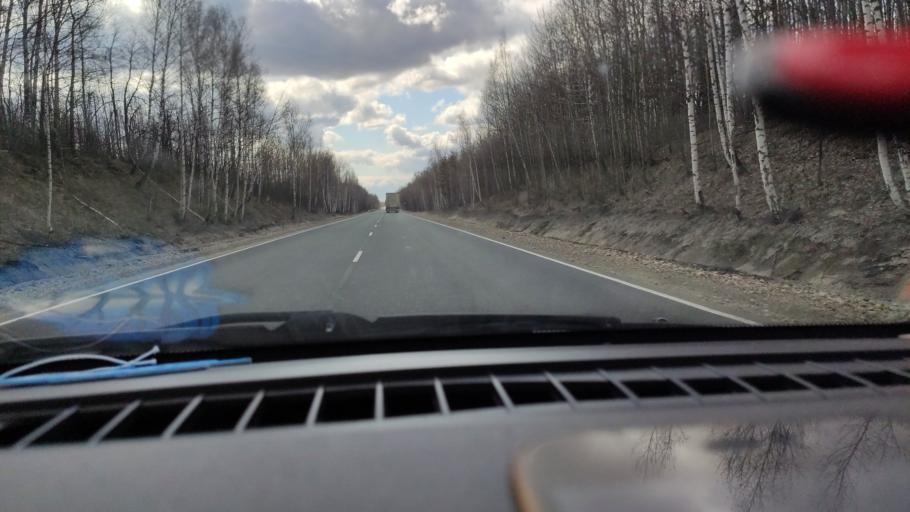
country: RU
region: Saratov
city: Khvalynsk
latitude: 52.4343
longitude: 48.0091
